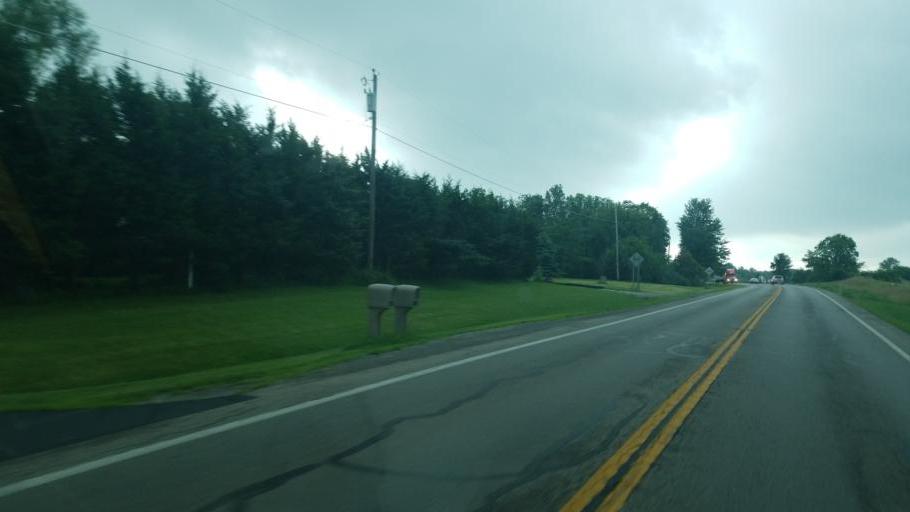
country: US
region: Ohio
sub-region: Logan County
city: Russells Point
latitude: 40.5557
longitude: -83.8350
